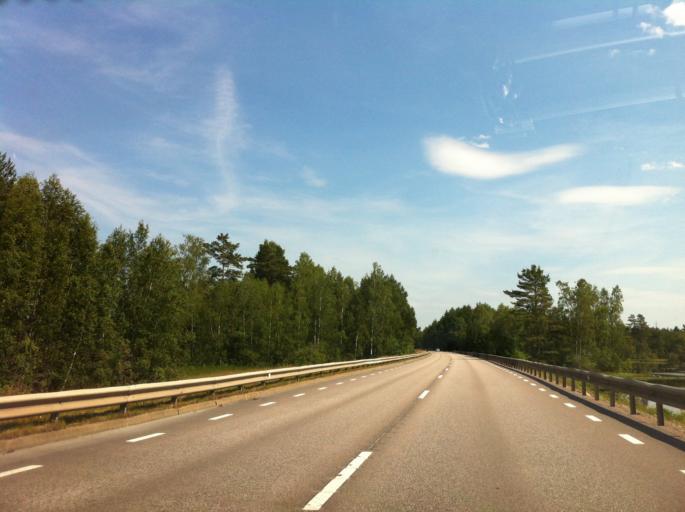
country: SE
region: Kalmar
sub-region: Nybro Kommun
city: Nybro
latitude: 56.8436
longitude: 15.7066
